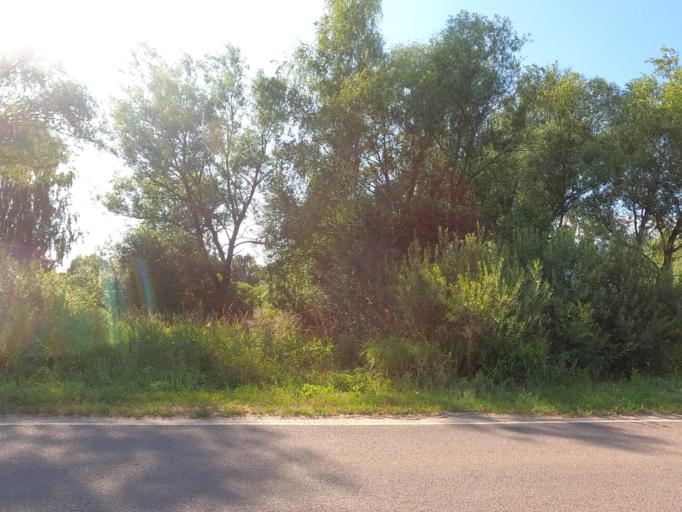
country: RU
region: Moskovskaya
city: Lopatinskiy
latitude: 55.3955
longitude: 38.7175
